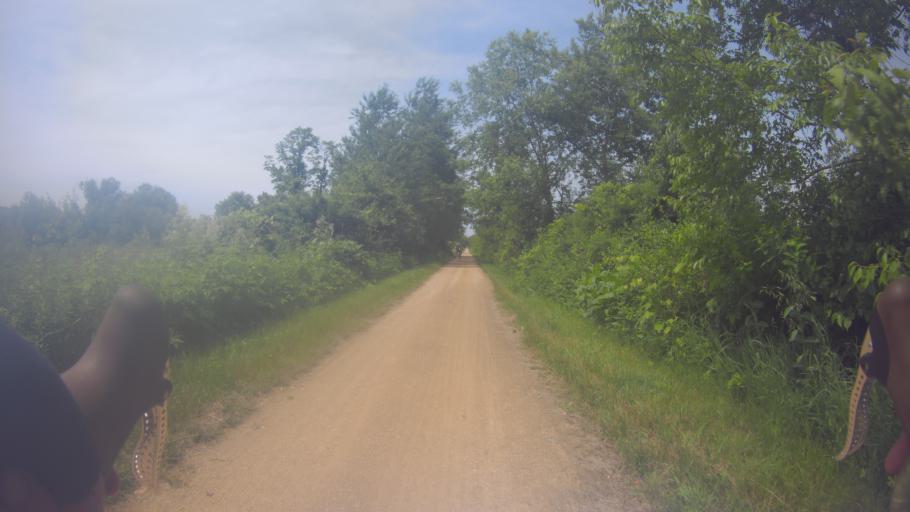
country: US
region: Wisconsin
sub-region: Dane County
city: Mount Horeb
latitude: 43.0275
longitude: -89.6610
